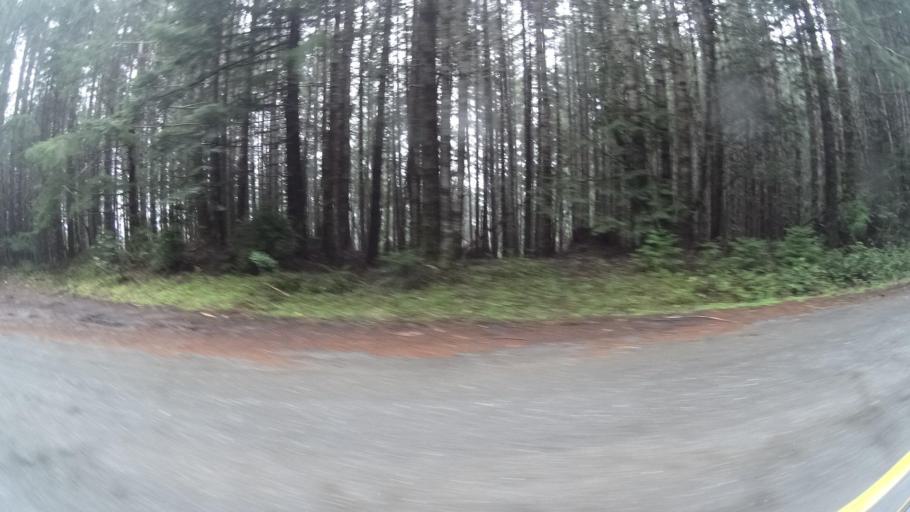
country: US
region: California
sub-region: Humboldt County
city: Westhaven-Moonstone
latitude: 41.2508
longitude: -123.9855
